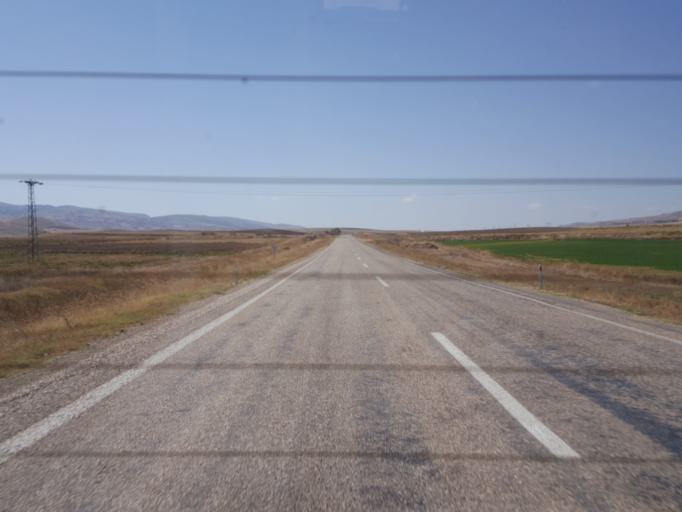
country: TR
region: Amasya
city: Dogantepe
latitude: 40.5757
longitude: 35.5994
